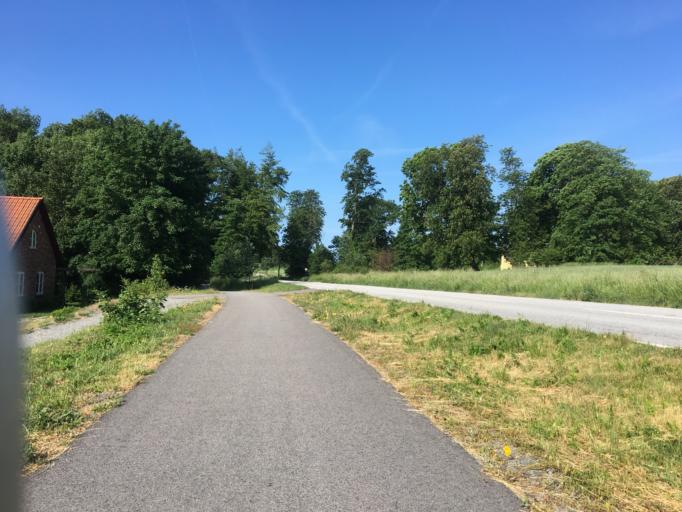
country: SE
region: Skane
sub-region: Ystads Kommun
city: Ystad
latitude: 55.4247
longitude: 13.7002
